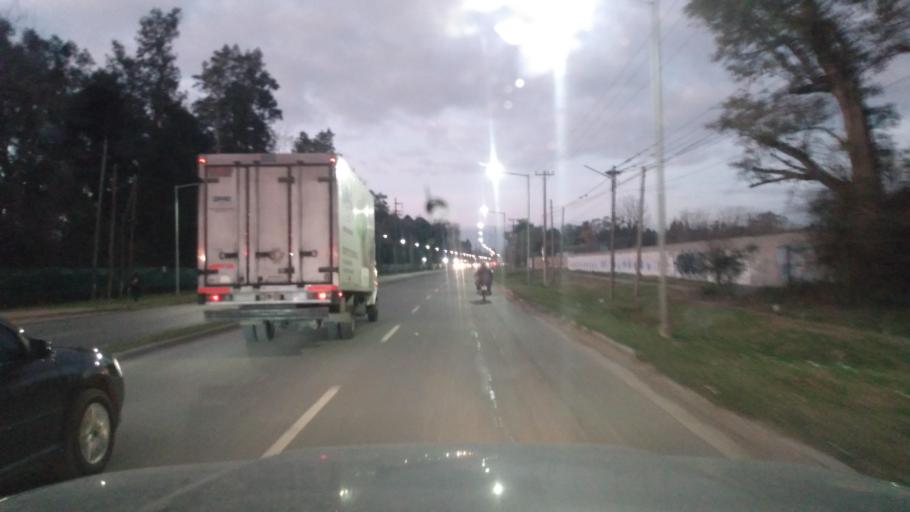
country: AR
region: Buenos Aires
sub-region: Partido de Pilar
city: Pilar
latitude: -34.4421
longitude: -58.8993
